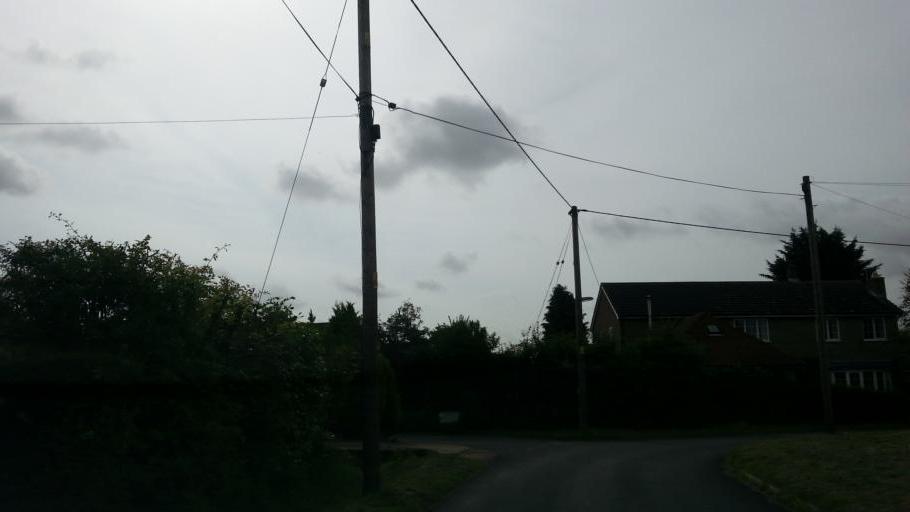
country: GB
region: England
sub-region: Cambridgeshire
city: Comberton
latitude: 52.1871
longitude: 0.0271
